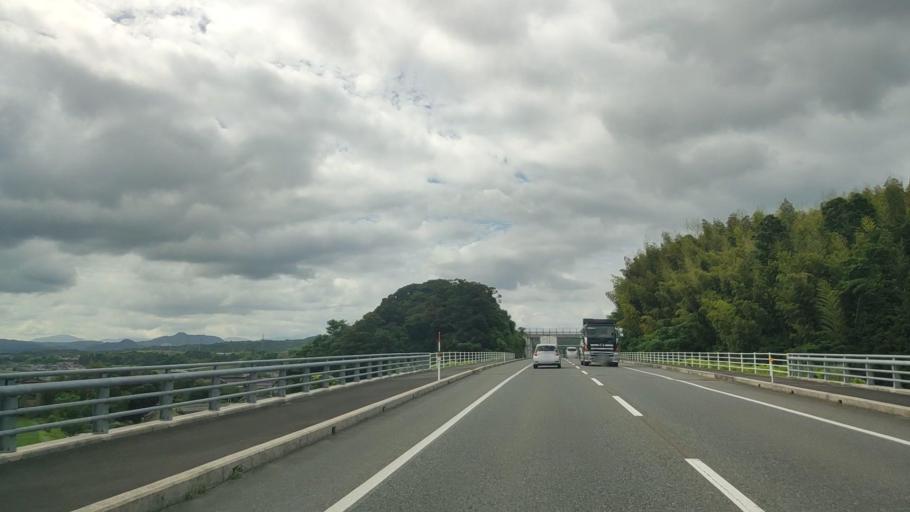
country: JP
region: Tottori
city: Yonago
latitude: 35.3932
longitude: 133.3822
